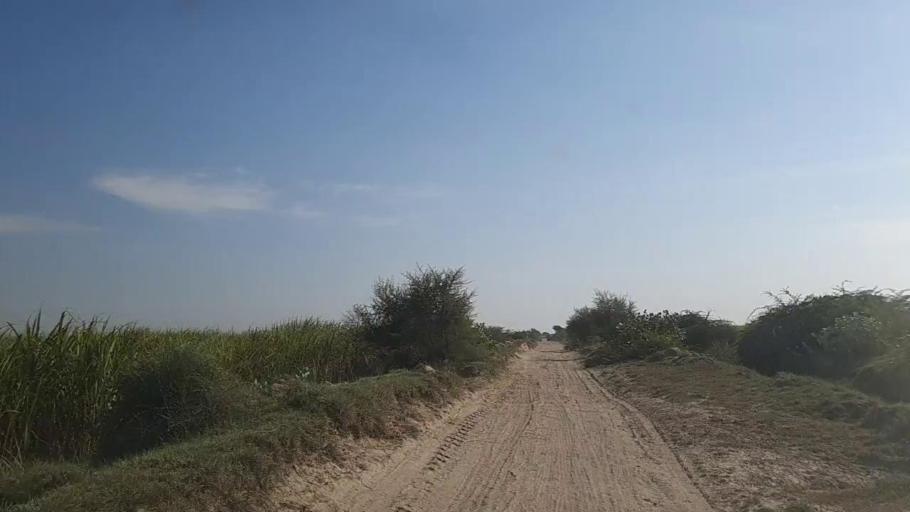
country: PK
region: Sindh
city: Bulri
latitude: 24.8505
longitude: 68.2901
